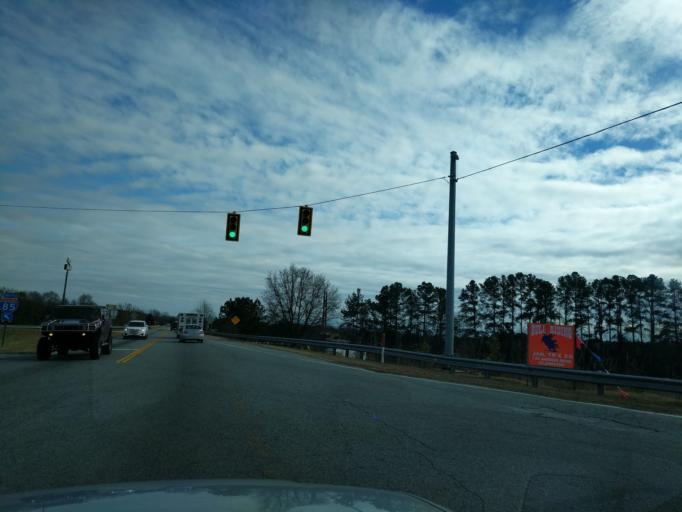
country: US
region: Georgia
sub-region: Hart County
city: Reed Creek
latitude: 34.5289
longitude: -82.8456
